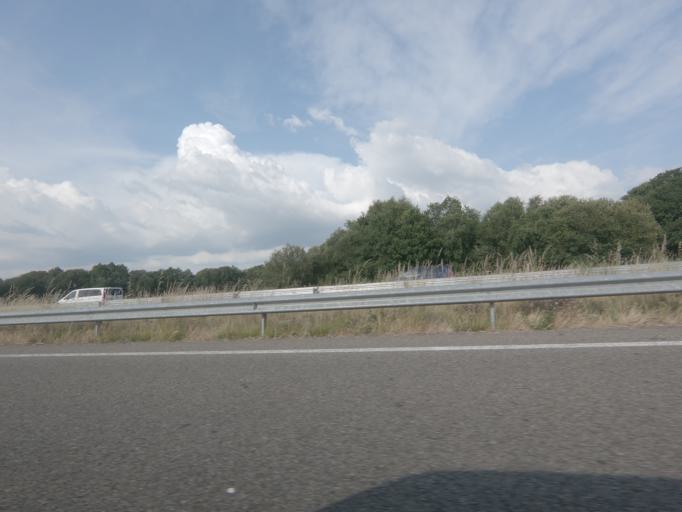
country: ES
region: Galicia
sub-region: Provincia de Ourense
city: Xinzo de Limia
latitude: 42.1307
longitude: -7.7417
